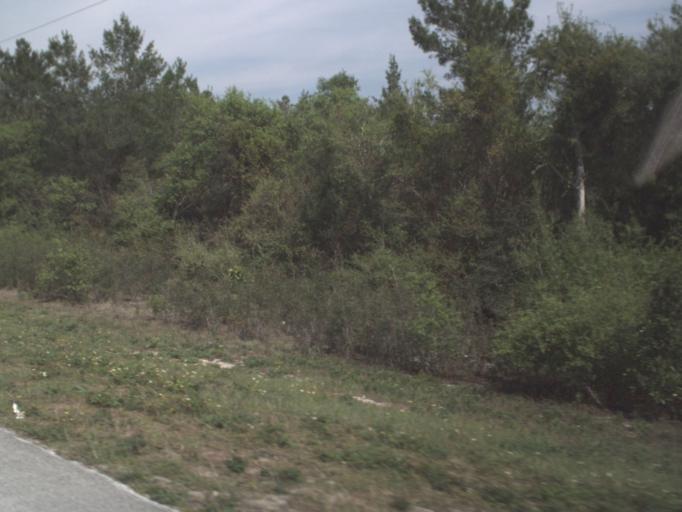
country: US
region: Florida
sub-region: Lake County
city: Astor
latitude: 29.2958
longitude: -81.6606
